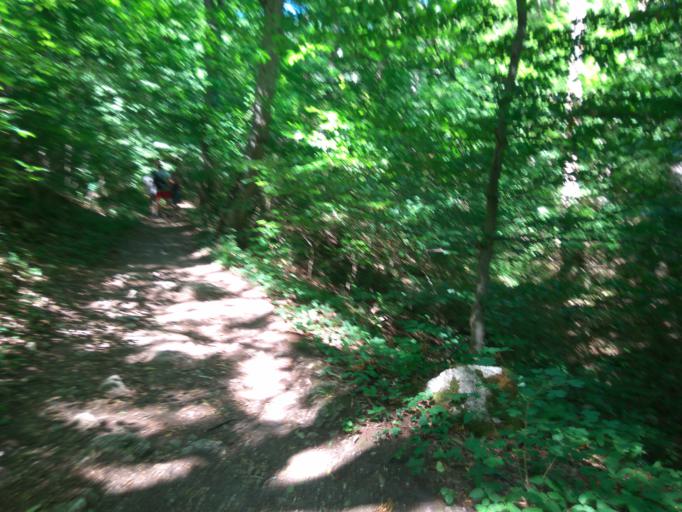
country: HU
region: Veszprem
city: Balatonfured
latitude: 46.9949
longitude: 17.8811
